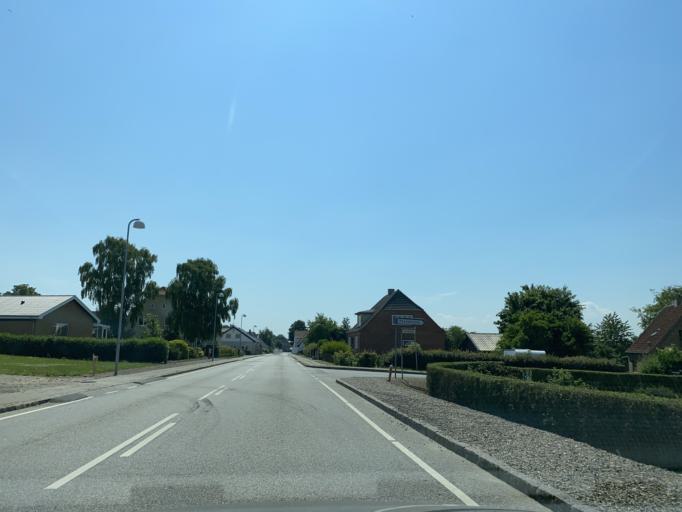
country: DK
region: South Denmark
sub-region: Sonderborg Kommune
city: Grasten
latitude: 54.9987
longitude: 9.5812
